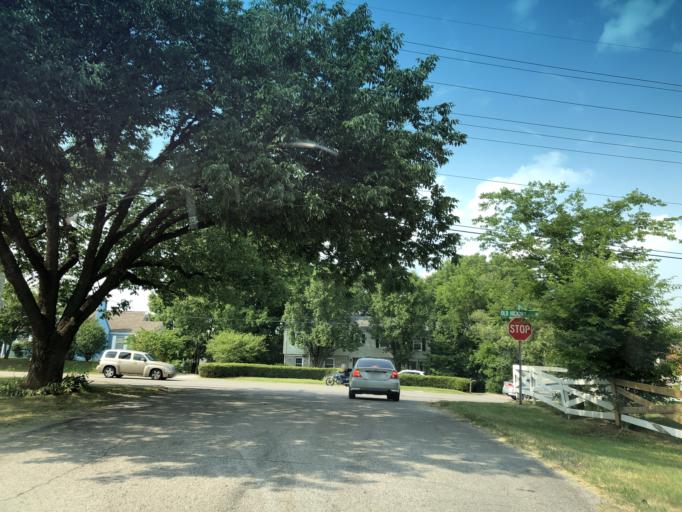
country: US
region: Tennessee
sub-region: Davidson County
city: Goodlettsville
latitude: 36.2636
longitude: -86.7211
